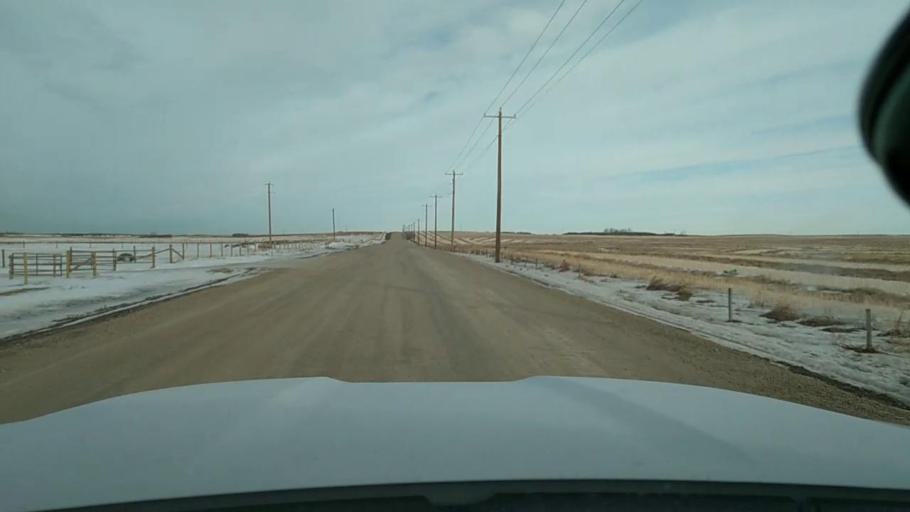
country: CA
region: Alberta
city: Airdrie
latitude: 51.2324
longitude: -113.9118
